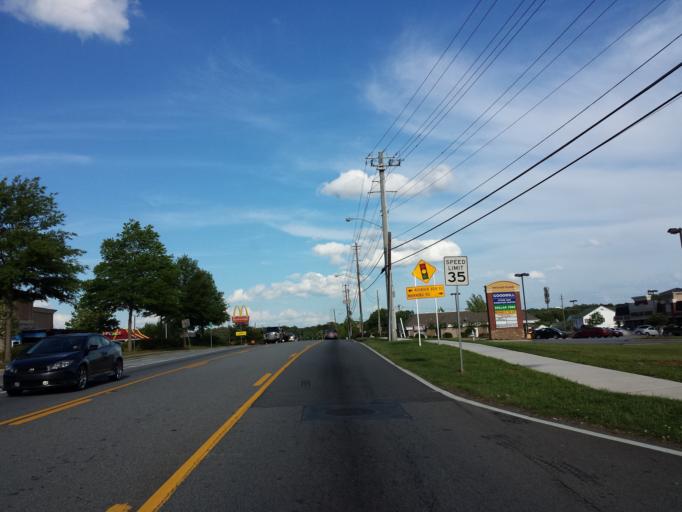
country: US
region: Georgia
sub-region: Cobb County
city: Marietta
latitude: 33.9520
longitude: -84.5767
